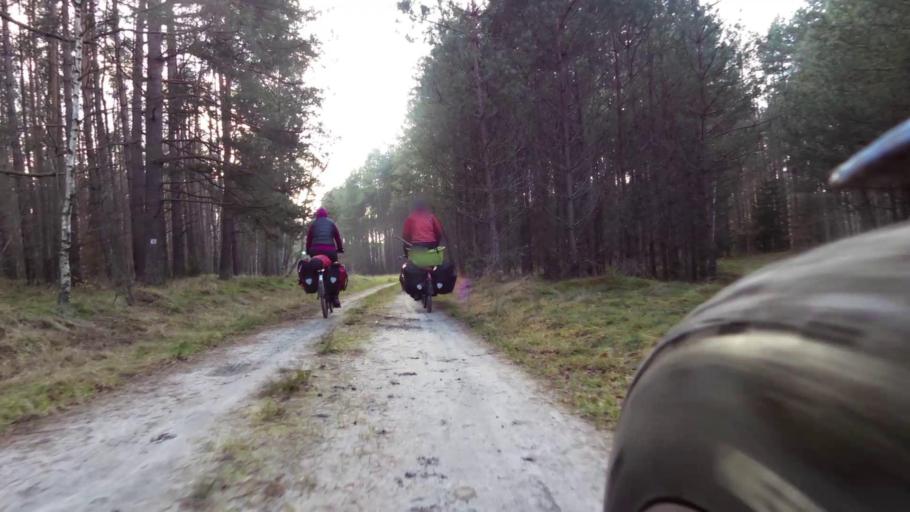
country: PL
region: West Pomeranian Voivodeship
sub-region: Powiat szczecinecki
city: Borne Sulinowo
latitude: 53.6142
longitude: 16.6186
